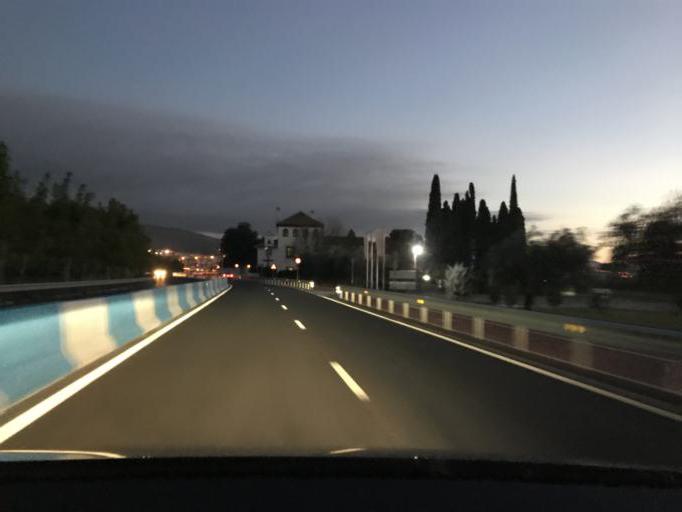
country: ES
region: Andalusia
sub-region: Provincia de Granada
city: Cajar
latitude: 37.1407
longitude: -3.5903
